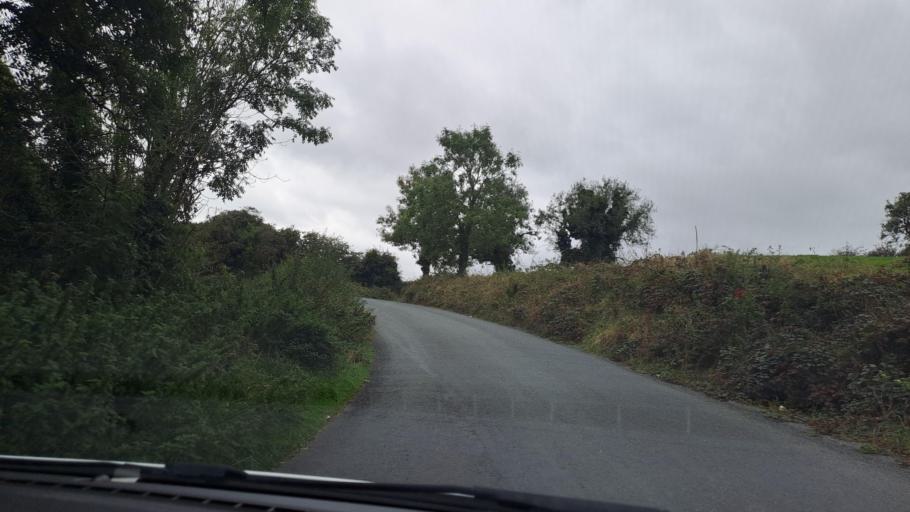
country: IE
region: Ulster
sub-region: An Cabhan
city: Kingscourt
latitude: 54.0185
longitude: -6.8685
